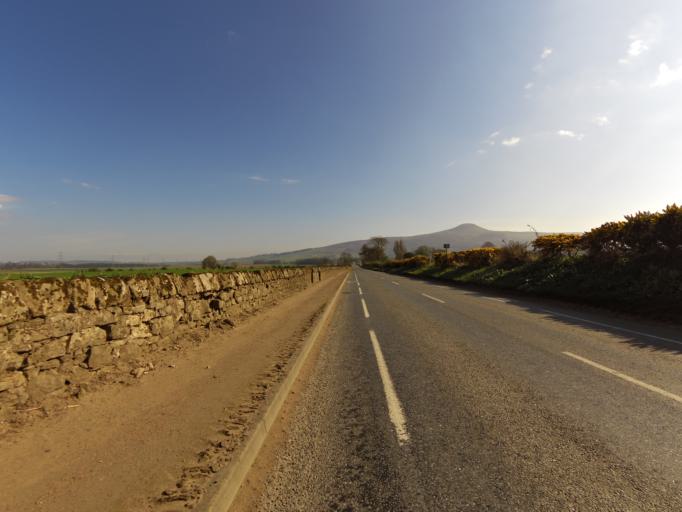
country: GB
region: Scotland
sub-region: Fife
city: Falkland
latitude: 56.2759
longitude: -3.2127
